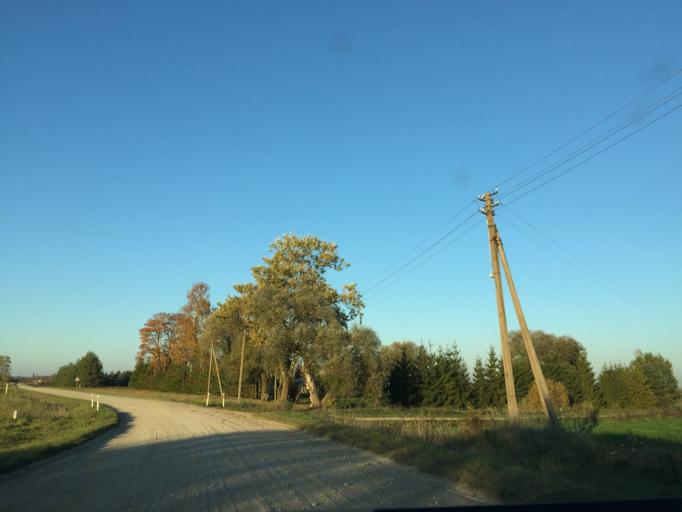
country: LT
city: Vieksniai
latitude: 56.3694
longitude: 22.5569
